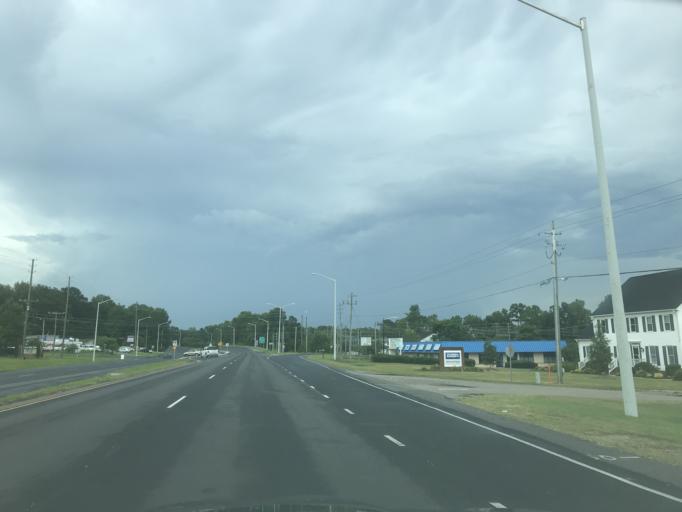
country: US
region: North Carolina
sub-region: Johnston County
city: Clayton
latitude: 35.6488
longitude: -78.4681
